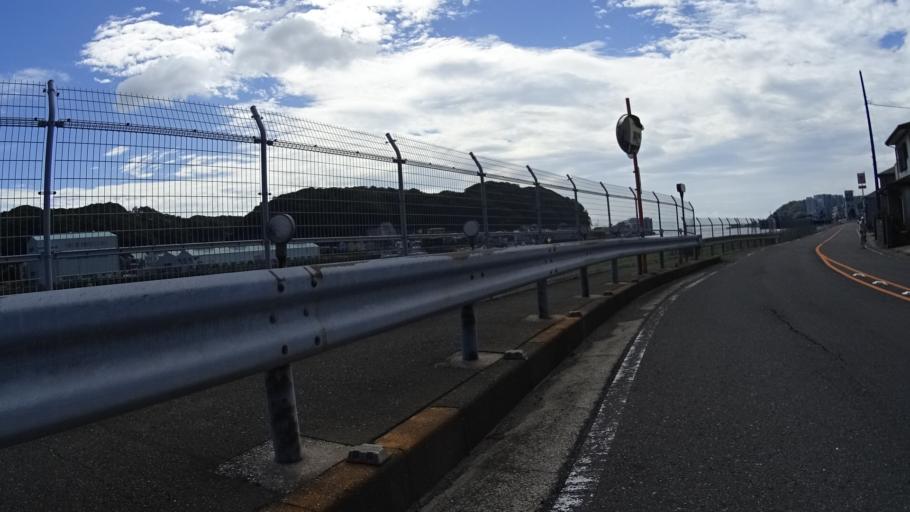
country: JP
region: Kanagawa
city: Yokosuka
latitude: 35.2444
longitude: 139.7175
